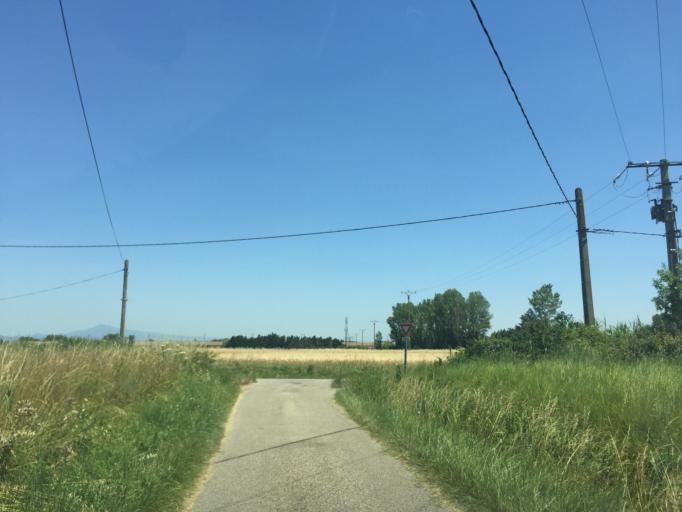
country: FR
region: Provence-Alpes-Cote d'Azur
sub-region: Departement du Vaucluse
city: Caderousse
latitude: 44.1097
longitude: 4.7684
